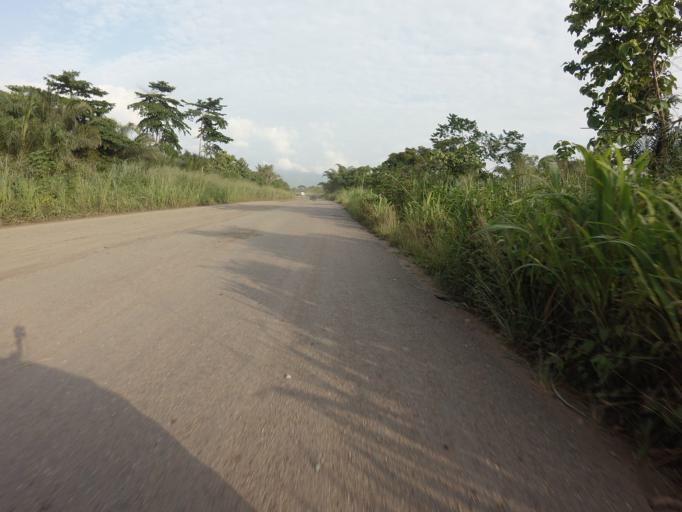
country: GH
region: Volta
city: Kpandu
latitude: 6.9778
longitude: 0.4489
